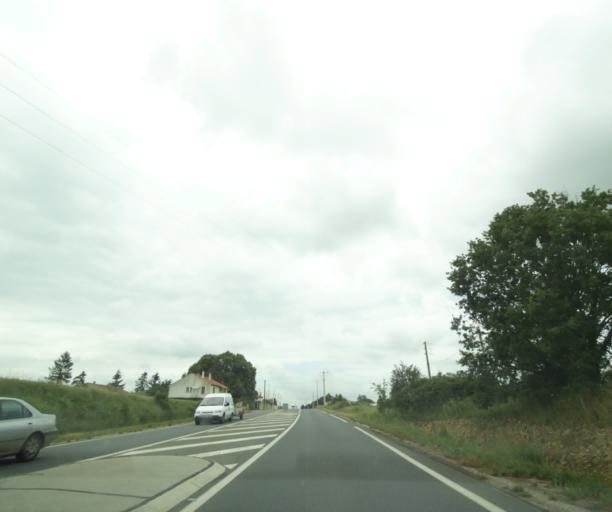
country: FR
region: Poitou-Charentes
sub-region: Departement des Deux-Sevres
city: Saint-Varent
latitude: 46.9197
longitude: -0.1963
